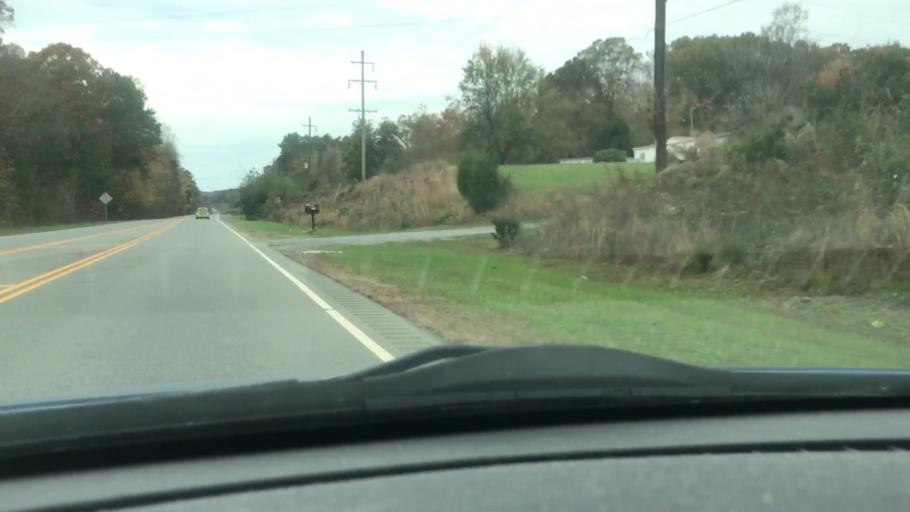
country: US
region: North Carolina
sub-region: Davidson County
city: Thomasville
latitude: 35.7593
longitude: -80.0573
